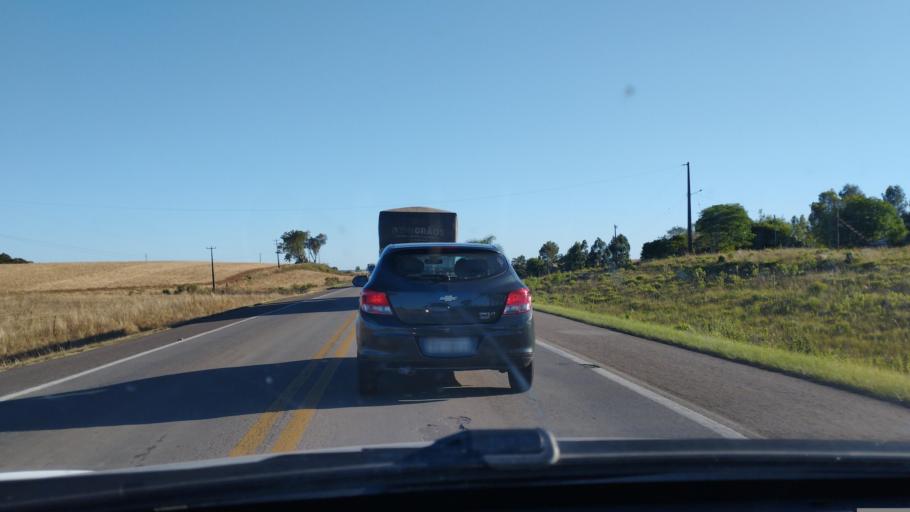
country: BR
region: Rio Grande do Sul
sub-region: Julio De Castilhos
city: Julio de Castilhos
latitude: -29.3796
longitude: -53.6704
